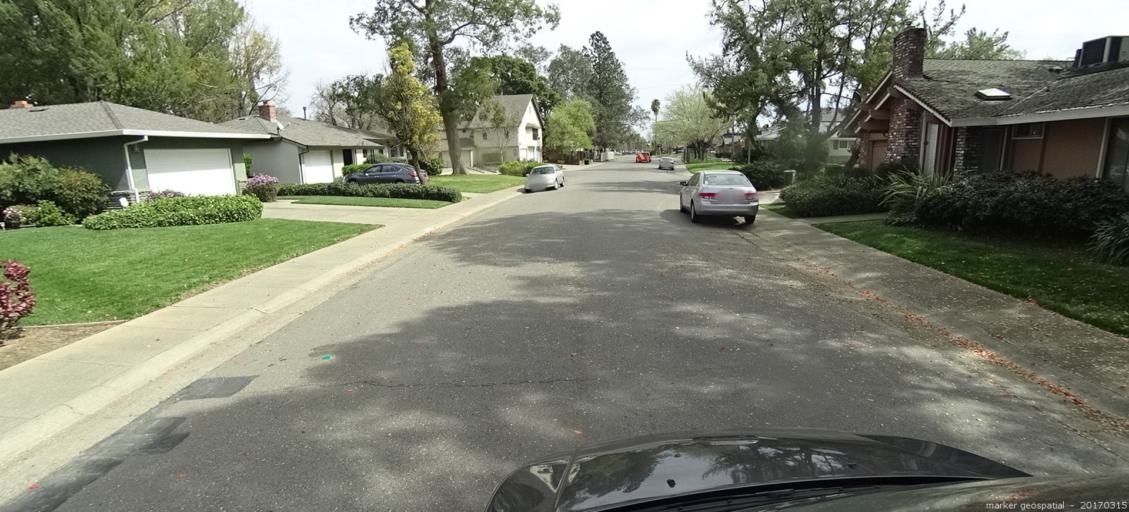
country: US
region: California
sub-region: Sacramento County
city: Parkway
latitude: 38.5165
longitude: -121.4854
